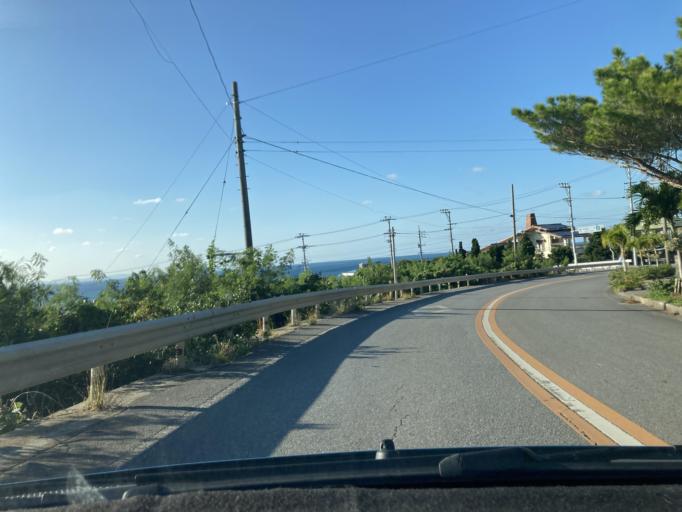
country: JP
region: Okinawa
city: Itoman
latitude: 26.1055
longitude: 127.6649
